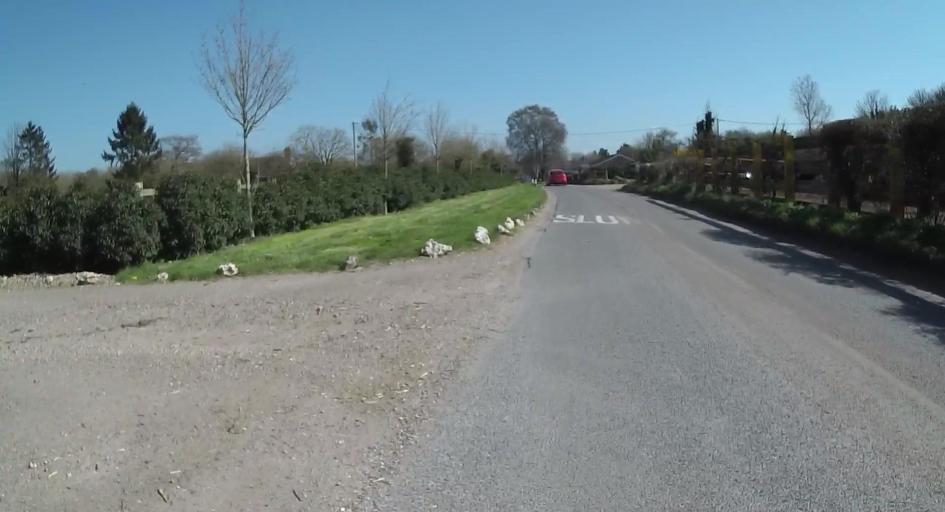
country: GB
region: England
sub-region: Hampshire
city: Andover
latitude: 51.2668
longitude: -1.4274
